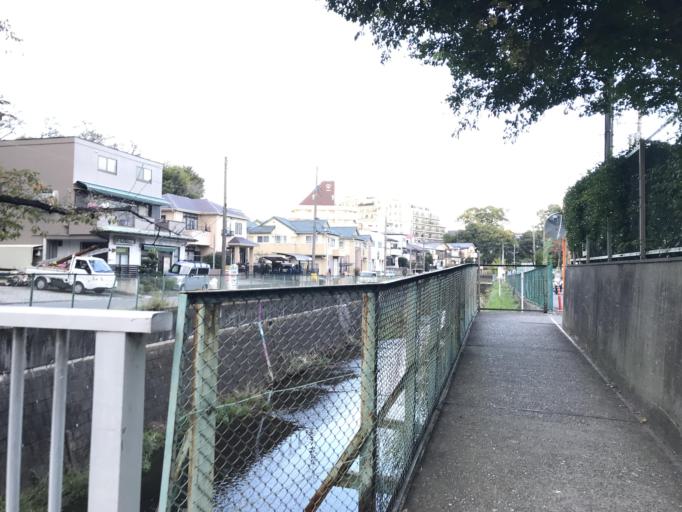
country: JP
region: Saitama
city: Wako
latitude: 35.7694
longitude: 139.6115
